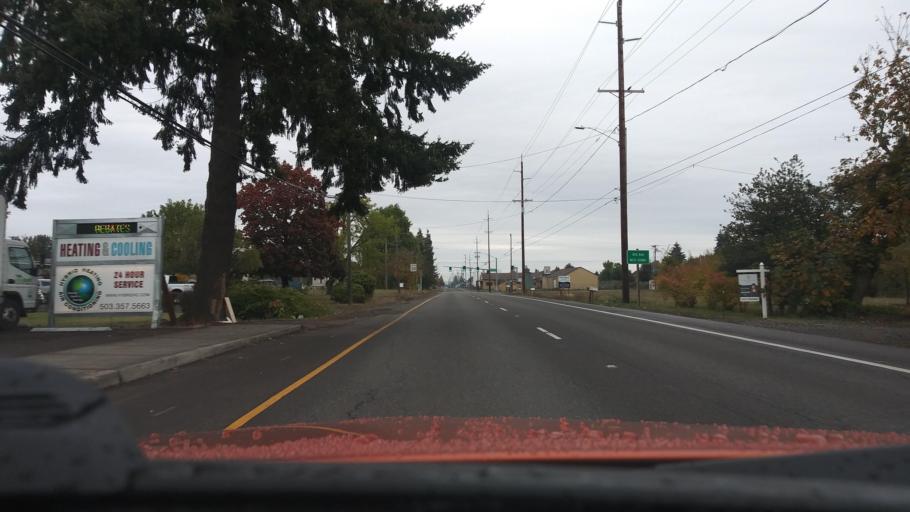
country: US
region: Oregon
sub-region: Washington County
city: Cornelius
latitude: 45.5201
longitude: -123.0690
